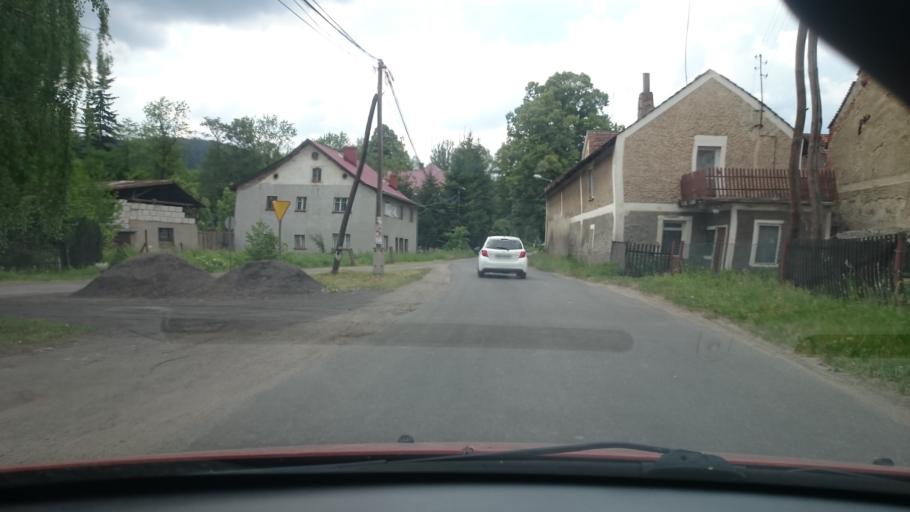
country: PL
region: Lower Silesian Voivodeship
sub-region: Powiat klodzki
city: Bystrzyca Klodzka
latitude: 50.3027
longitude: 16.6236
